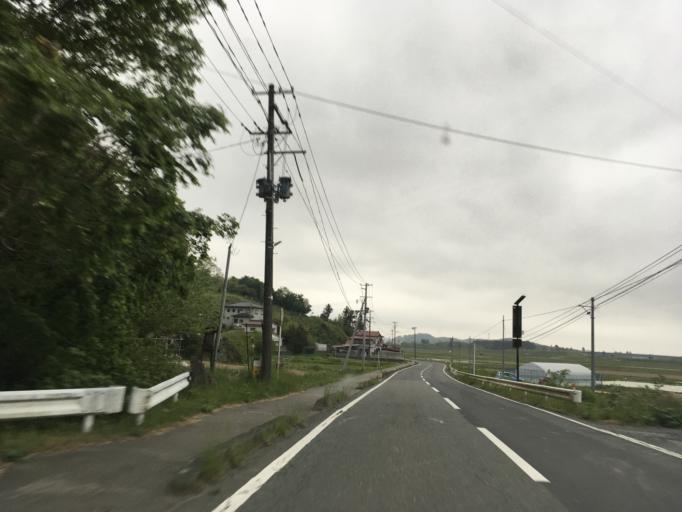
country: JP
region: Miyagi
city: Wakuya
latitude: 38.7289
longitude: 141.2979
